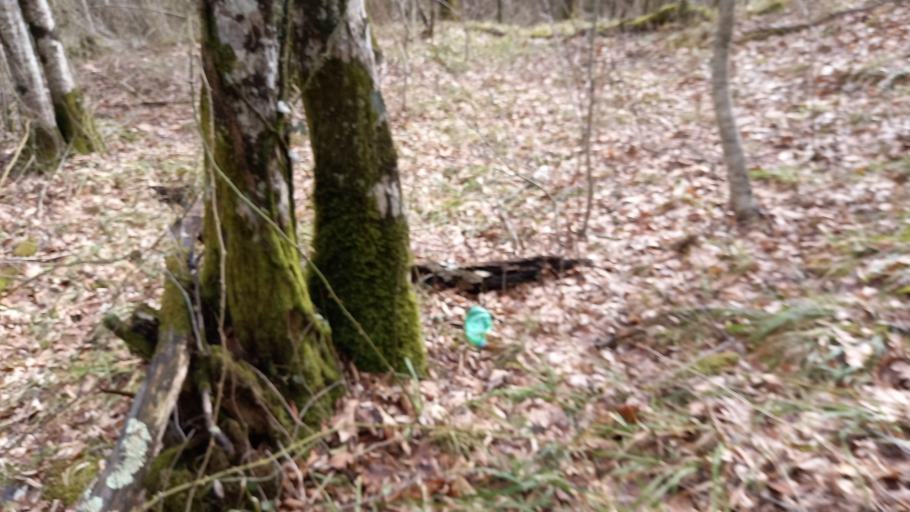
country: RU
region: Krasnodarskiy
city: Dzhubga
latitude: 44.4027
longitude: 38.7071
